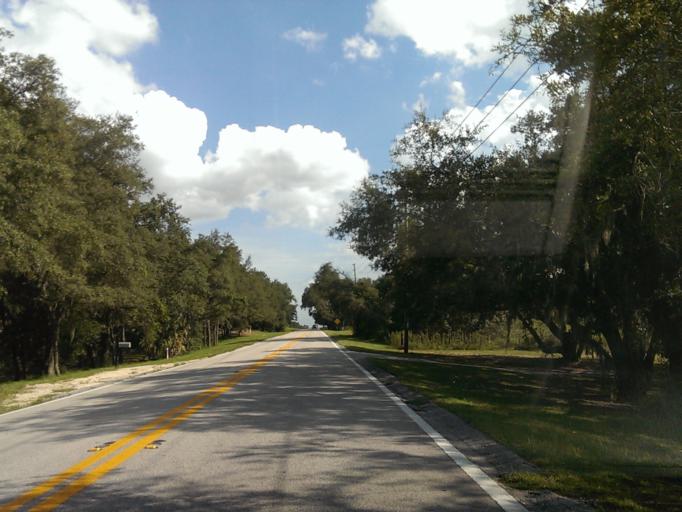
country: US
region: Florida
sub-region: Orange County
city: Oakland
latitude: 28.4876
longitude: -81.6407
